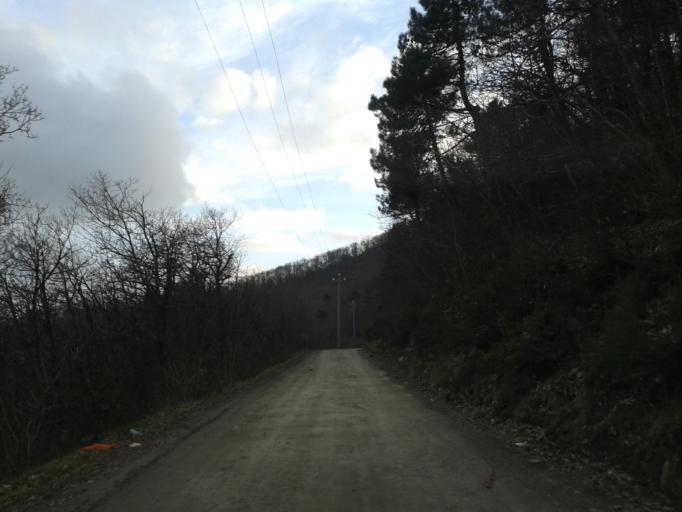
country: IT
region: Tuscany
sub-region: Province of Pisa
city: Calci
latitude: 43.7646
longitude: 10.5294
